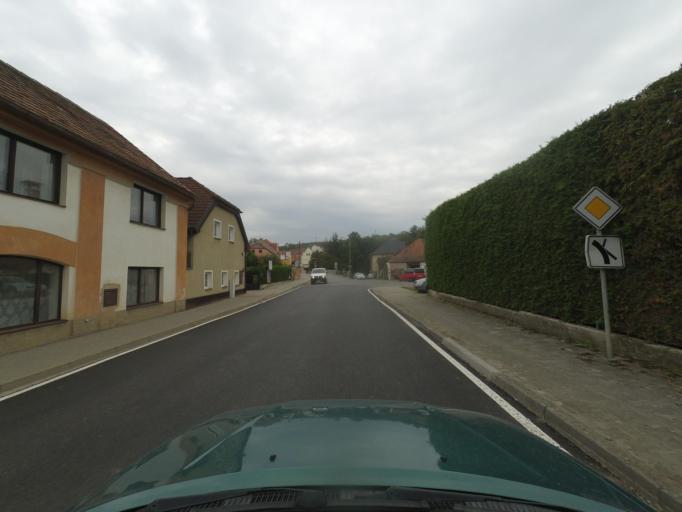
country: CZ
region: Plzensky
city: Merklin
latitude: 49.5594
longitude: 13.1957
